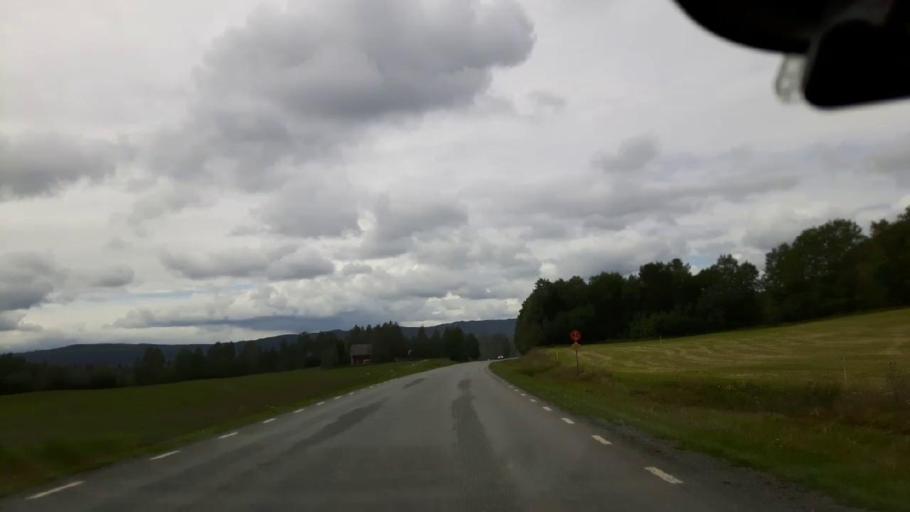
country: SE
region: Jaemtland
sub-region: Krokoms Kommun
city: Krokom
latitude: 63.4535
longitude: 14.1378
